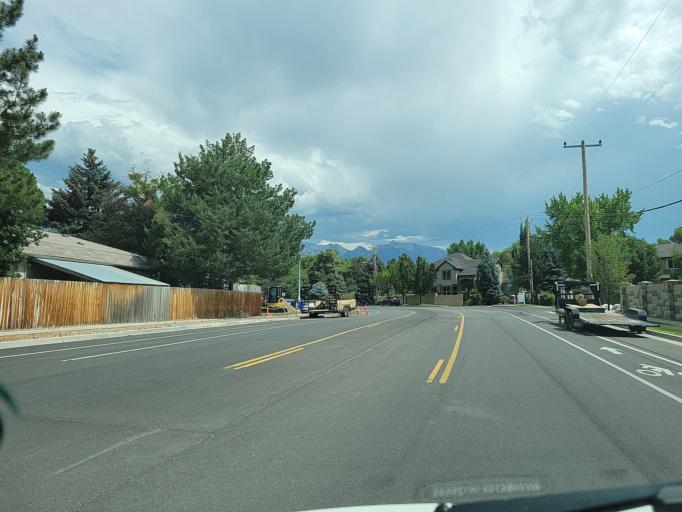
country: US
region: Utah
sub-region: Salt Lake County
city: Murray
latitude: 40.6413
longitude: -111.8628
